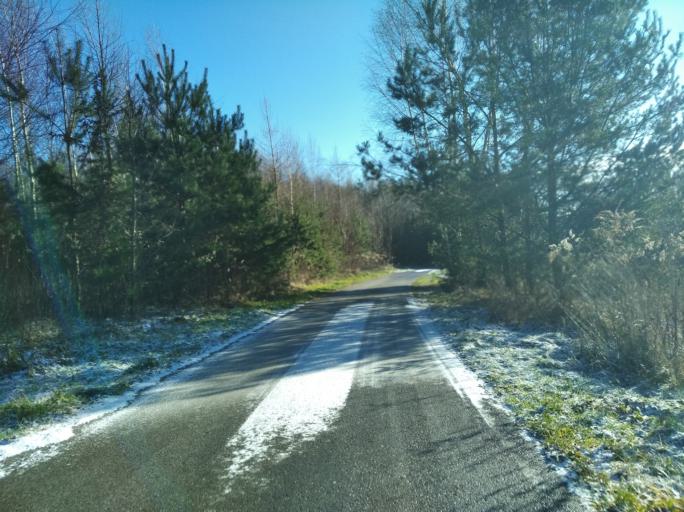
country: PL
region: Subcarpathian Voivodeship
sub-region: Powiat ropczycko-sedziszowski
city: Iwierzyce
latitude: 49.9599
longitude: 21.7523
